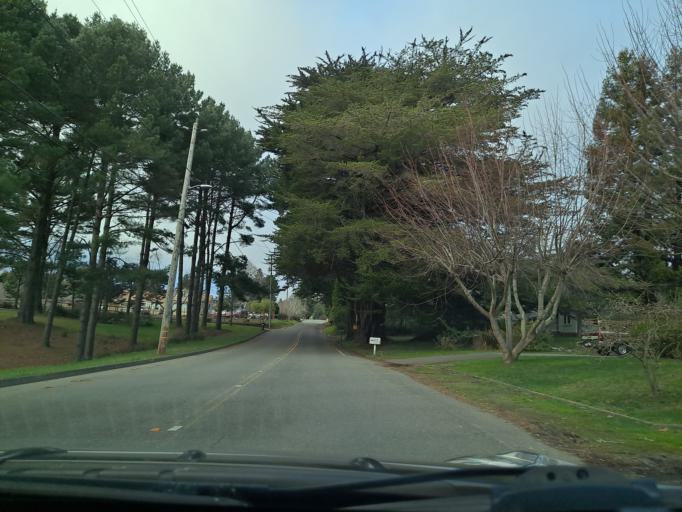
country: US
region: California
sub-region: Humboldt County
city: Fortuna
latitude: 40.6074
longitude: -124.1615
